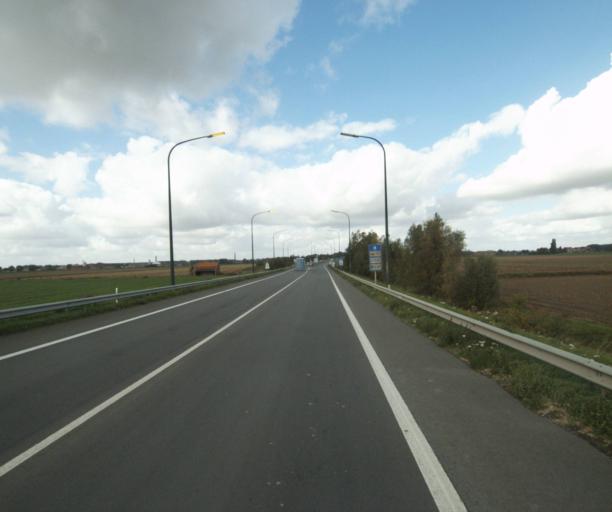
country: FR
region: Nord-Pas-de-Calais
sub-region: Departement du Nord
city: Houplines
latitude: 50.7063
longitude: 2.9210
